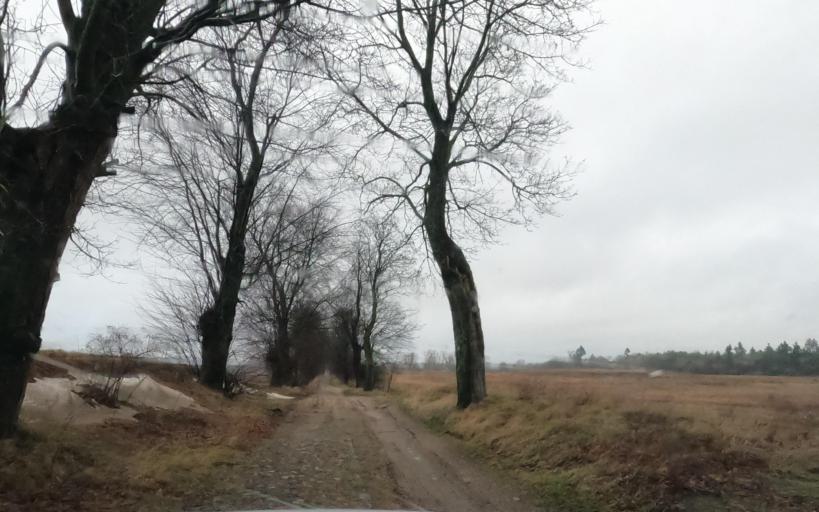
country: PL
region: West Pomeranian Voivodeship
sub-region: Powiat szczecinecki
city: Szczecinek
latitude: 53.6236
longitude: 16.6747
